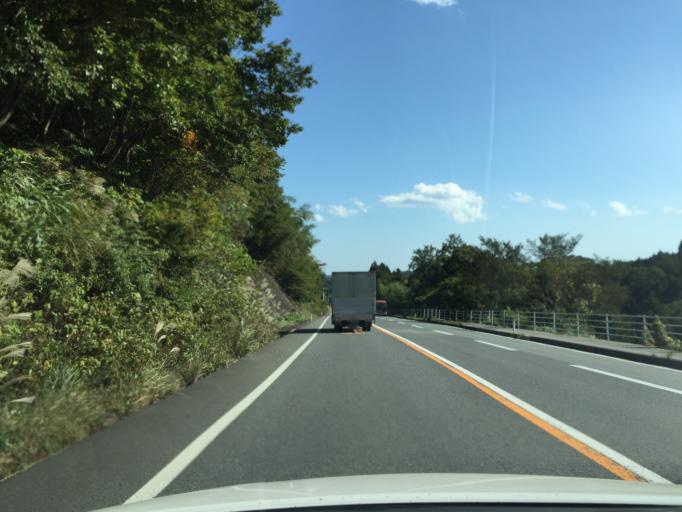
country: JP
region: Fukushima
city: Iwaki
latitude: 37.0780
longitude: 140.8177
